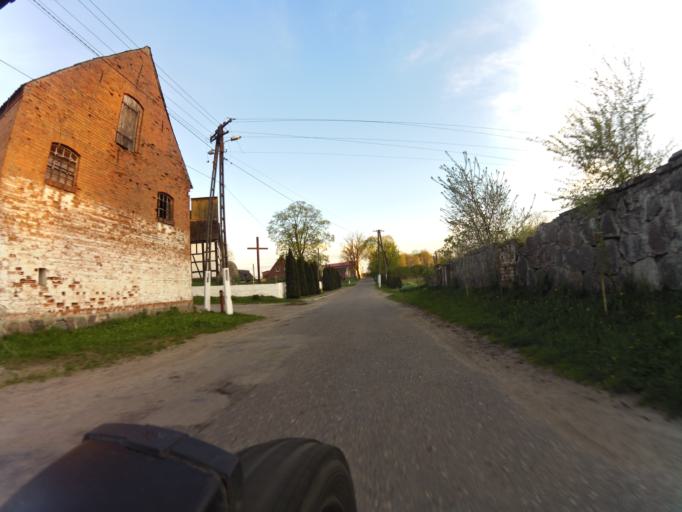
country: PL
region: West Pomeranian Voivodeship
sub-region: Powiat lobeski
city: Lobez
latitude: 53.6985
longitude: 15.6453
